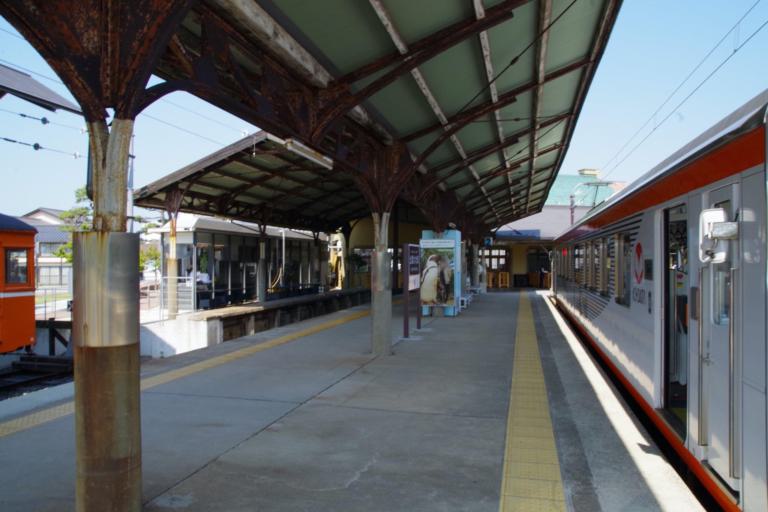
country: JP
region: Shimane
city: Izumo
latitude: 35.3934
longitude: 132.6875
